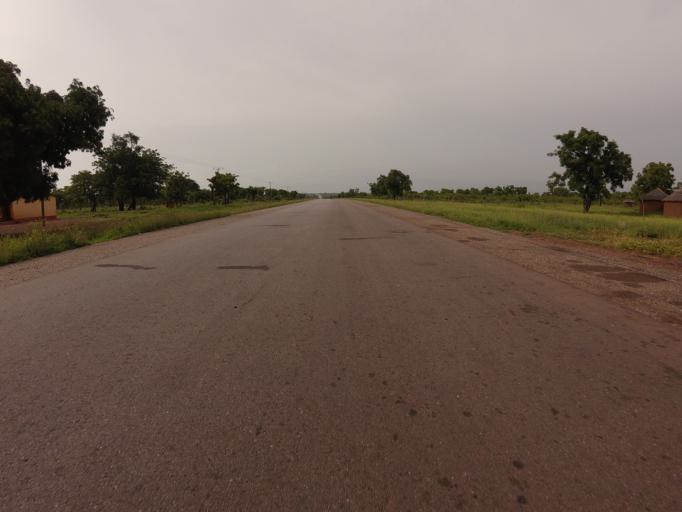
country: GH
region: Northern
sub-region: Yendi
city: Yendi
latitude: 9.6380
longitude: -0.0635
